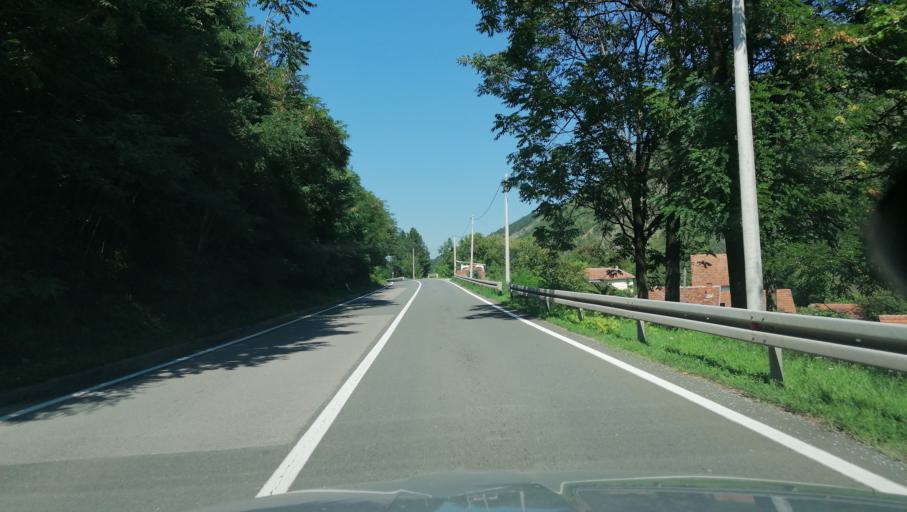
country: RS
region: Central Serbia
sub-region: Raski Okrug
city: Kraljevo
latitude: 43.6364
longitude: 20.5497
